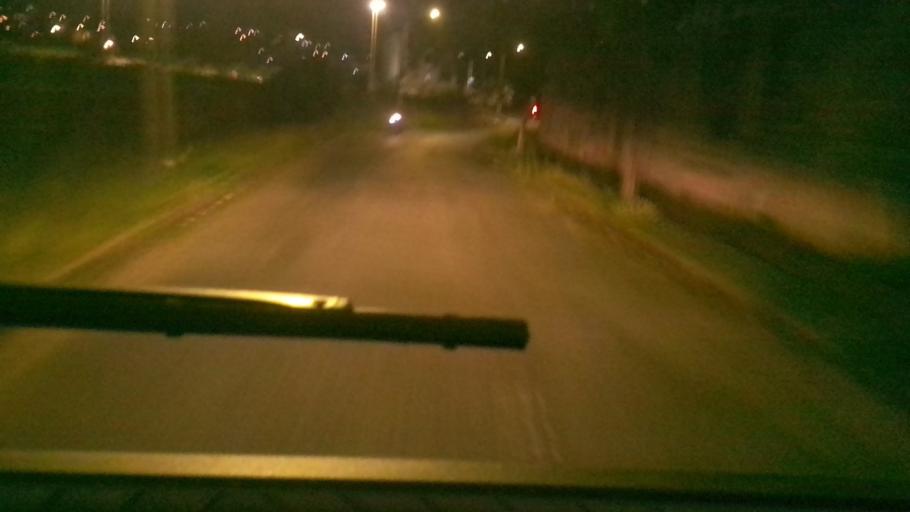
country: BR
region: Minas Gerais
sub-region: Belo Horizonte
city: Belo Horizonte
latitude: -19.8633
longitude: -43.9215
